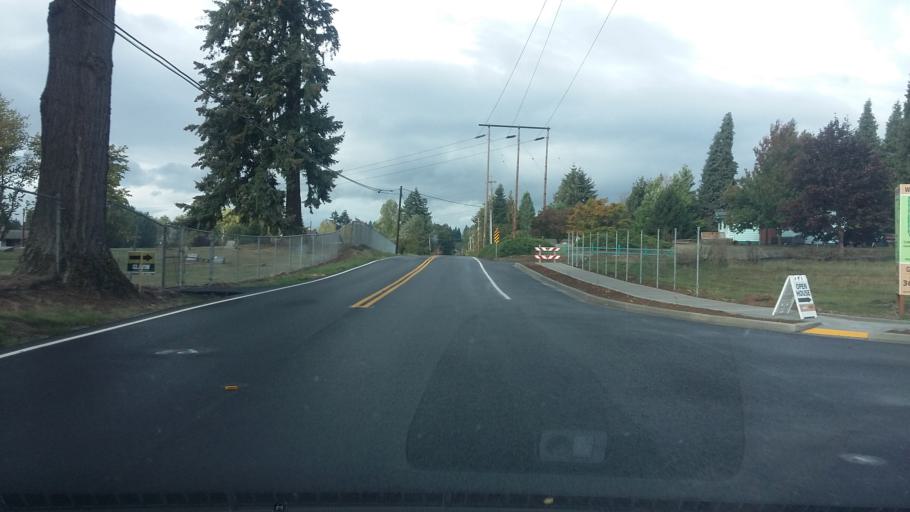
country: US
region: Washington
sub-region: Clark County
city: Barberton
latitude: 45.7005
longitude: -122.6082
